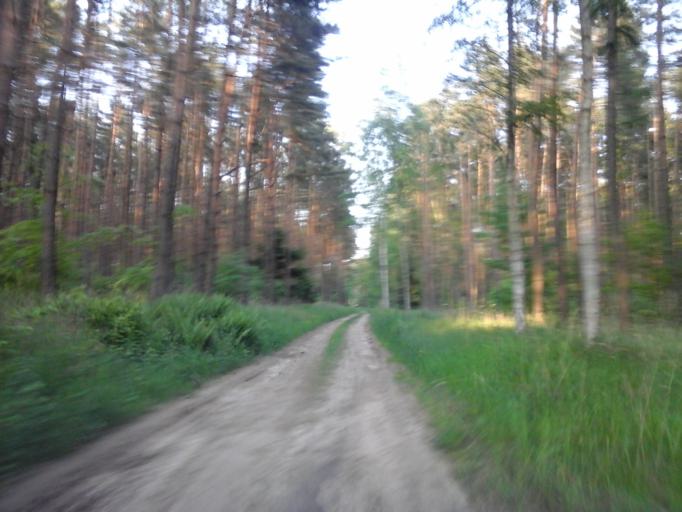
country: PL
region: West Pomeranian Voivodeship
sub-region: Powiat choszczenski
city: Krzecin
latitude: 53.0166
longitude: 15.5647
